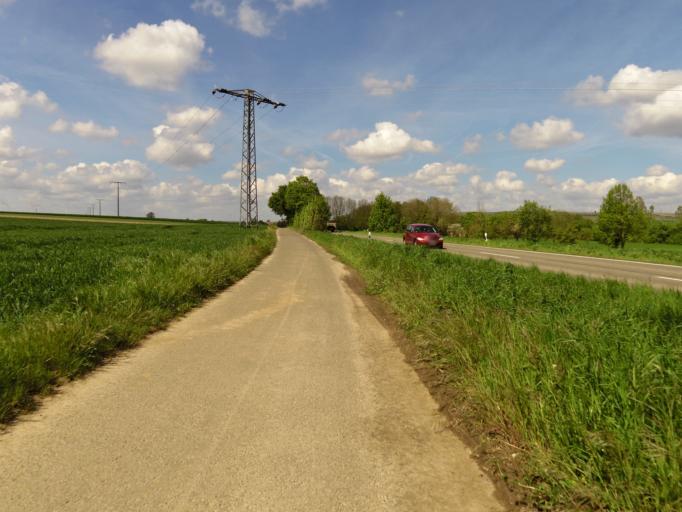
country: DE
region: Rheinland-Pfalz
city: Westhofen
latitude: 49.7052
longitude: 8.2714
